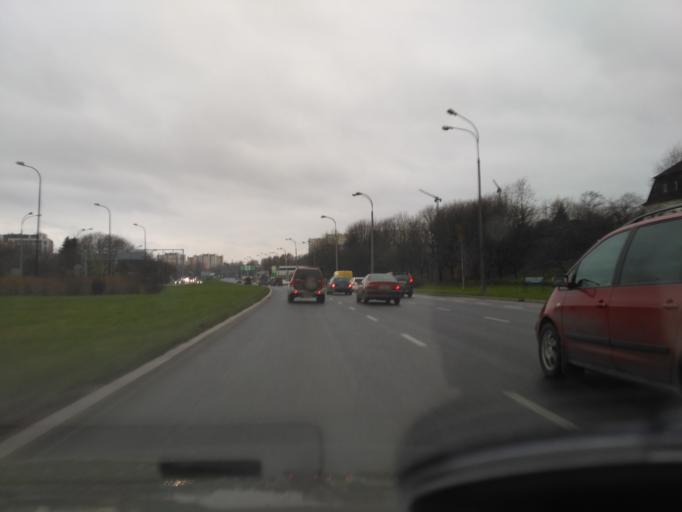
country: PL
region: Lublin Voivodeship
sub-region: Powiat lubelski
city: Lublin
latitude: 51.2533
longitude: 22.5607
